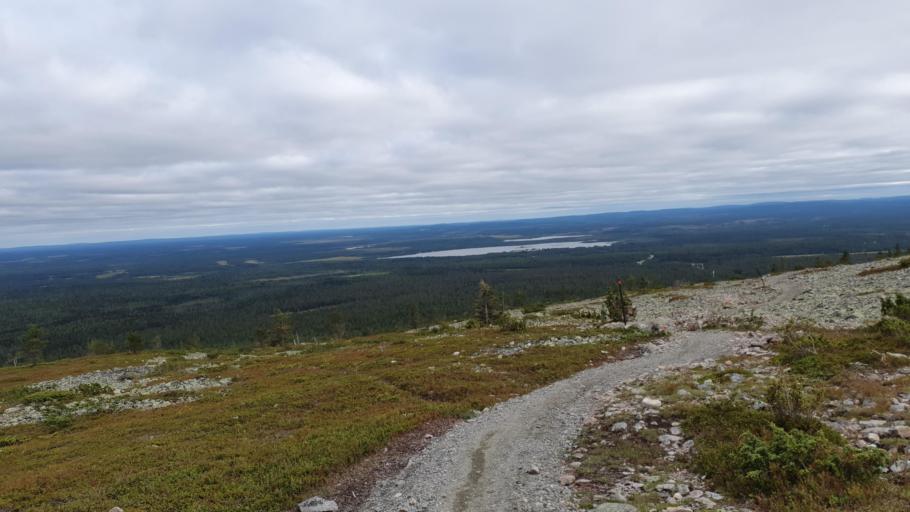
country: FI
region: Lapland
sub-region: Tunturi-Lappi
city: Kolari
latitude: 67.5655
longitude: 24.2509
